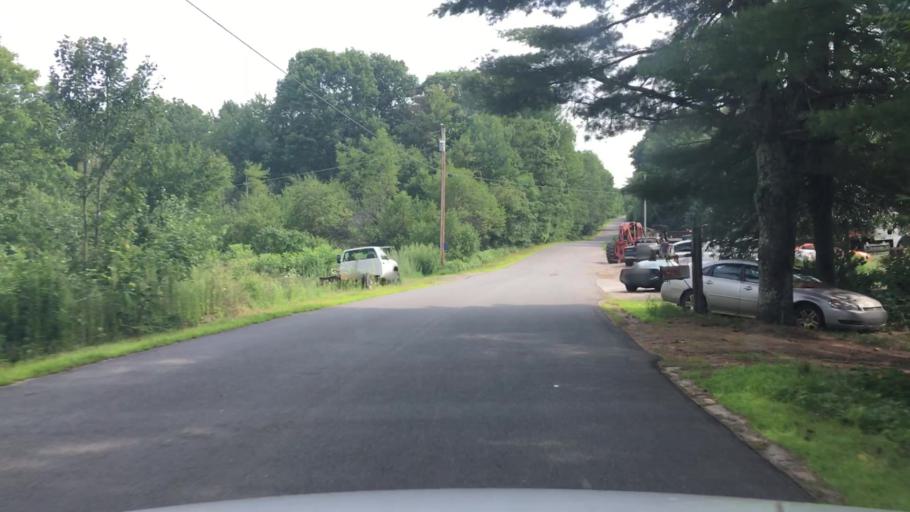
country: US
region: Maine
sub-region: Lincoln County
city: Jefferson
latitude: 44.2342
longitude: -69.4440
